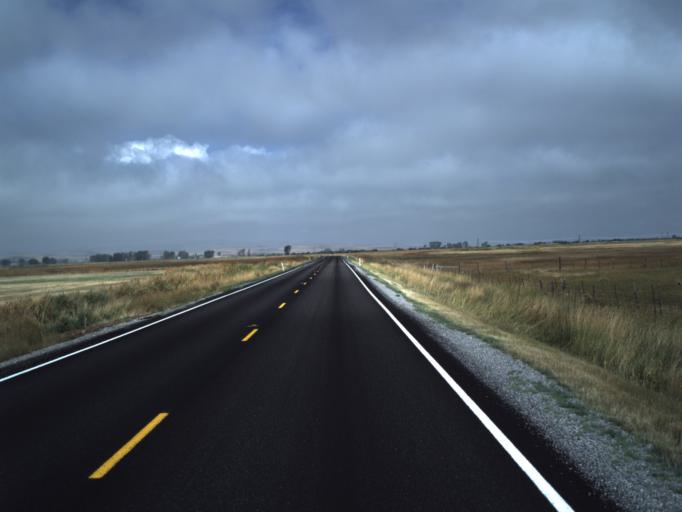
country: US
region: Utah
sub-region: Rich County
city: Randolph
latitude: 41.5054
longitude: -111.1259
